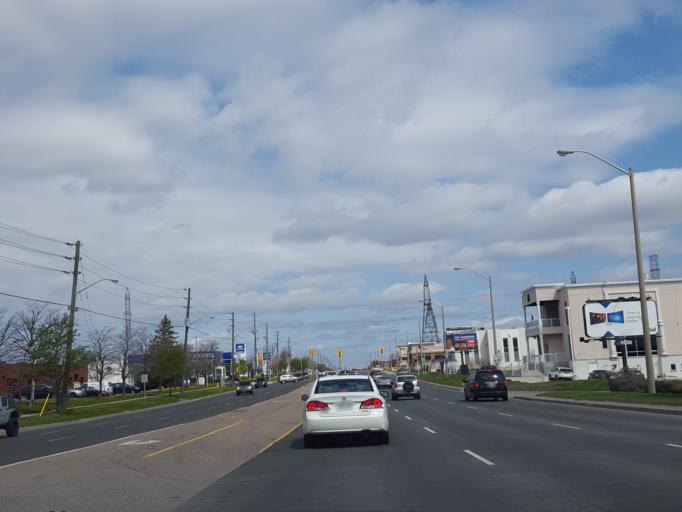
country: CA
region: Ontario
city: Scarborough
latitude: 43.8186
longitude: -79.2454
